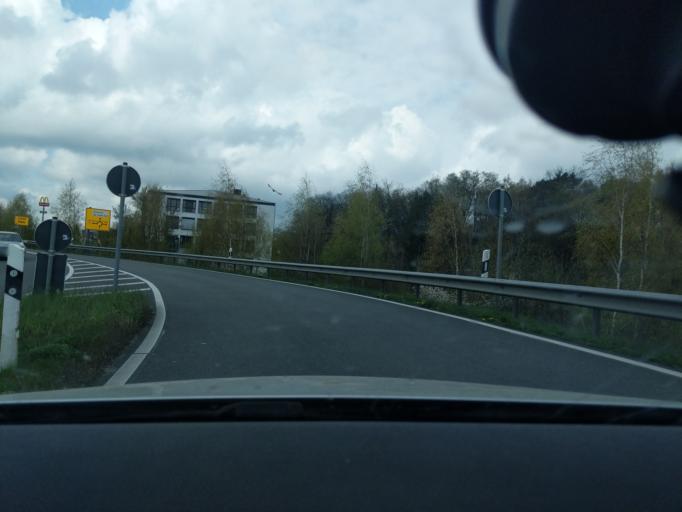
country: DE
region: Lower Saxony
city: Stade
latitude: 53.5824
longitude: 9.5028
